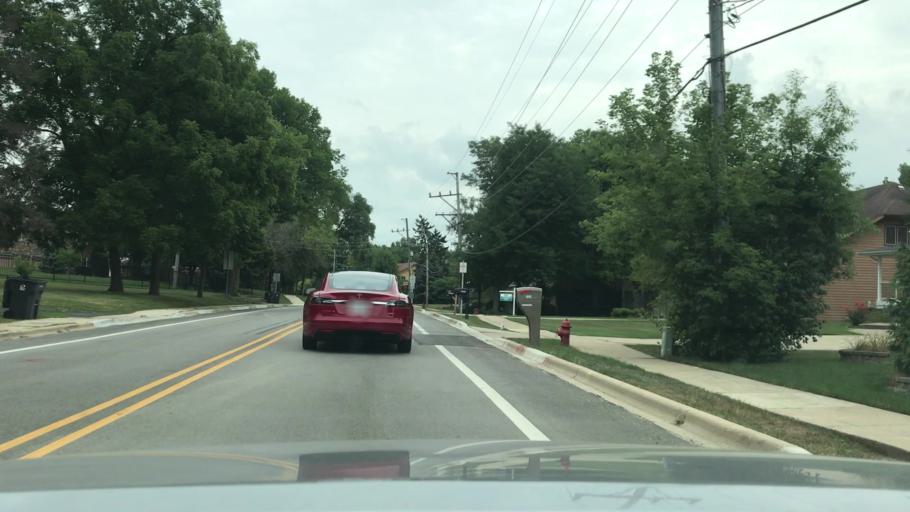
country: US
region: Illinois
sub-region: DuPage County
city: Darien
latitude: 41.7455
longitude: -87.9925
